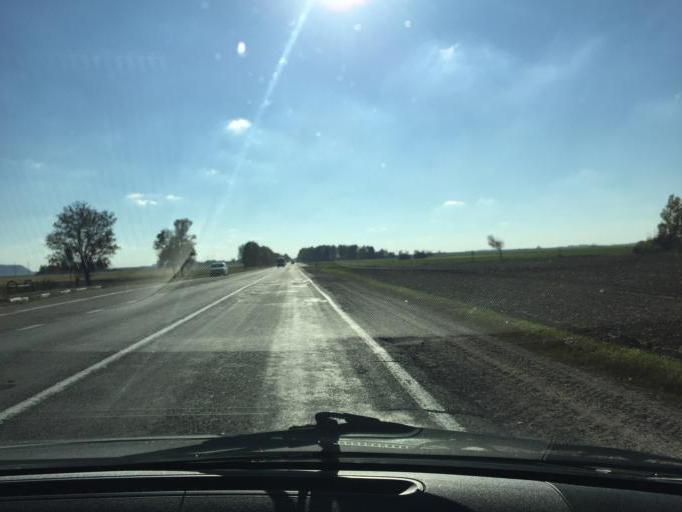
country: BY
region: Minsk
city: Slutsk
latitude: 52.9159
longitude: 27.4814
